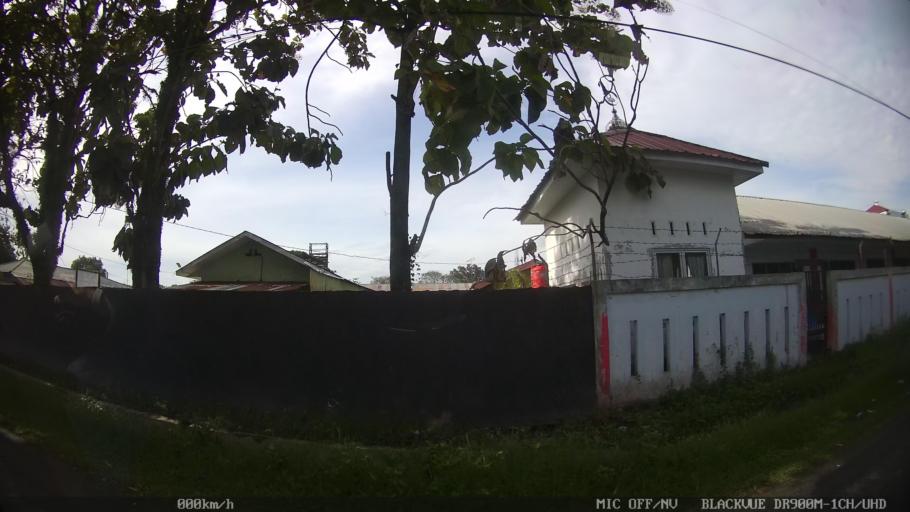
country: ID
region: North Sumatra
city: Medan
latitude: 3.6118
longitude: 98.6456
